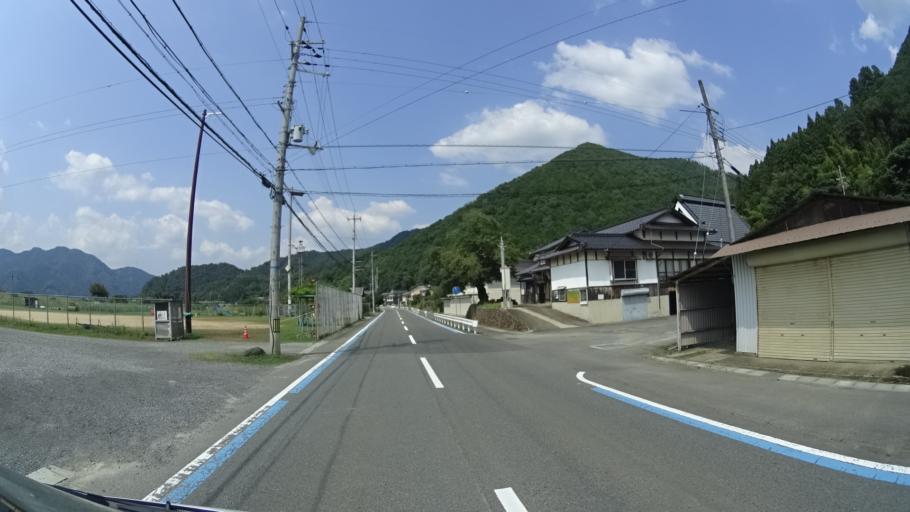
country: JP
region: Kyoto
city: Fukuchiyama
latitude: 35.3252
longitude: 135.1206
